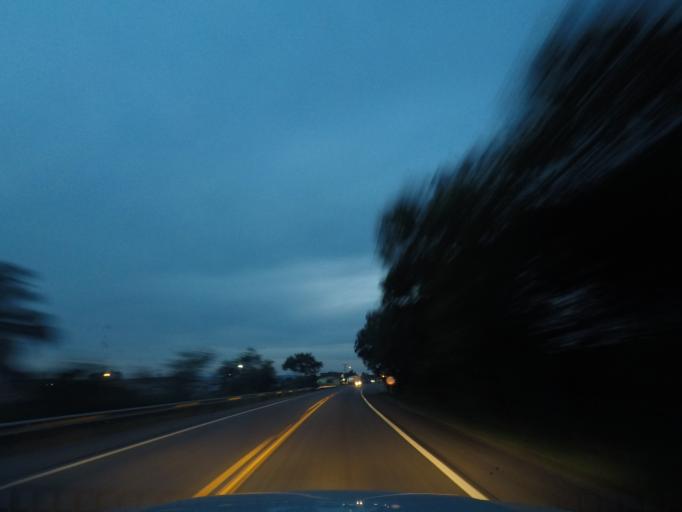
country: BR
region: Bahia
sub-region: Andarai
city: Vera Cruz
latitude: -12.5010
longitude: -41.2880
